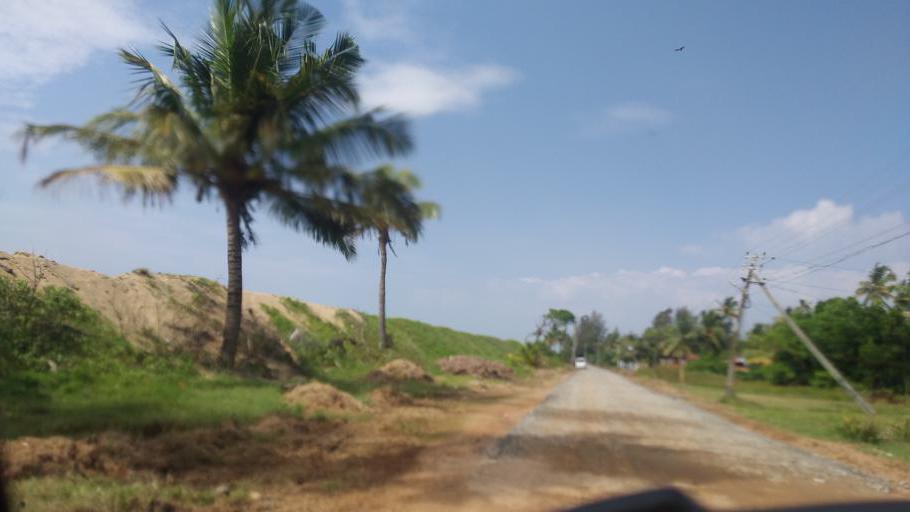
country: IN
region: Kerala
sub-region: Ernakulam
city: Elur
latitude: 10.0618
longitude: 76.1998
